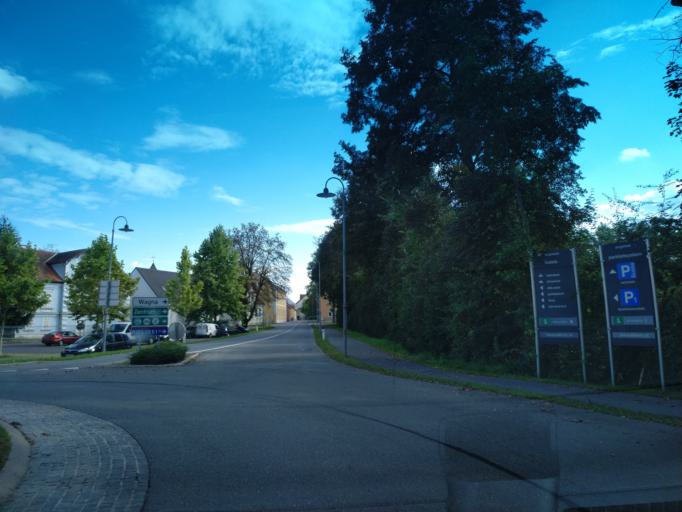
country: AT
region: Styria
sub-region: Politischer Bezirk Leibnitz
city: Leibnitz
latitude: 46.7839
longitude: 15.5352
